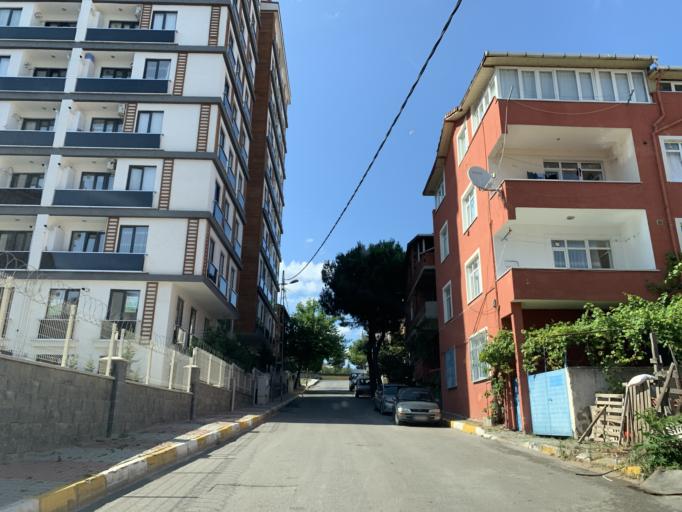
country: TR
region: Istanbul
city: Pendik
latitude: 40.8882
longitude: 29.2712
